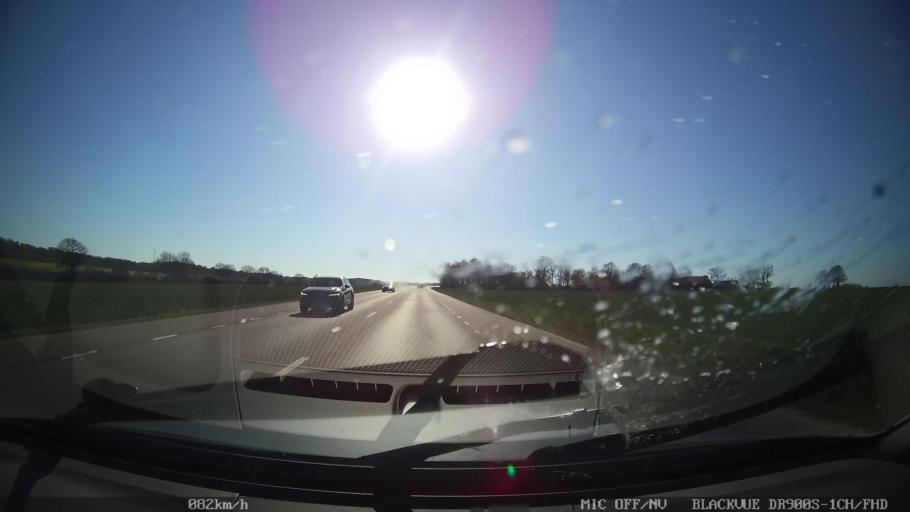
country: SE
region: Skane
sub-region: Helsingborg
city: Hyllinge
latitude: 56.1003
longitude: 12.8237
